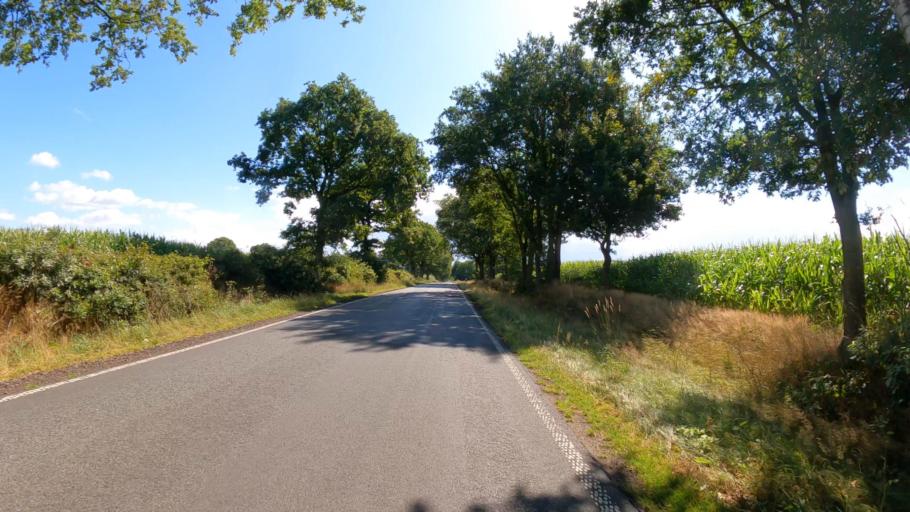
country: DE
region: Schleswig-Holstein
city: Armstedt
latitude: 53.9601
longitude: 9.8621
